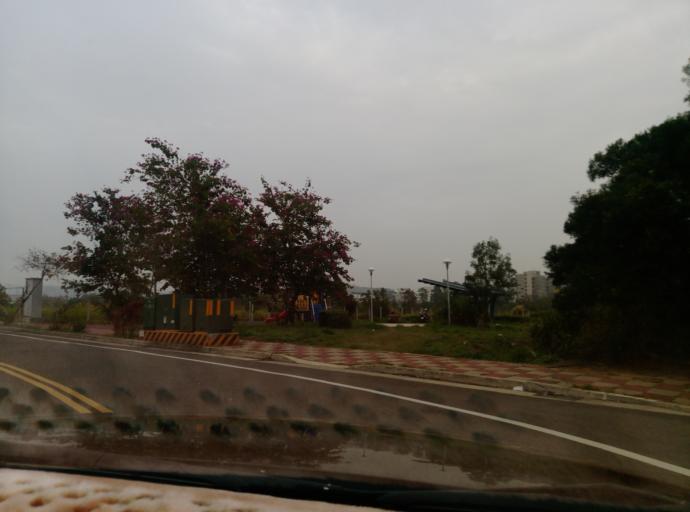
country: TW
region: Taiwan
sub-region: Hsinchu
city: Hsinchu
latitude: 24.7029
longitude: 120.9061
